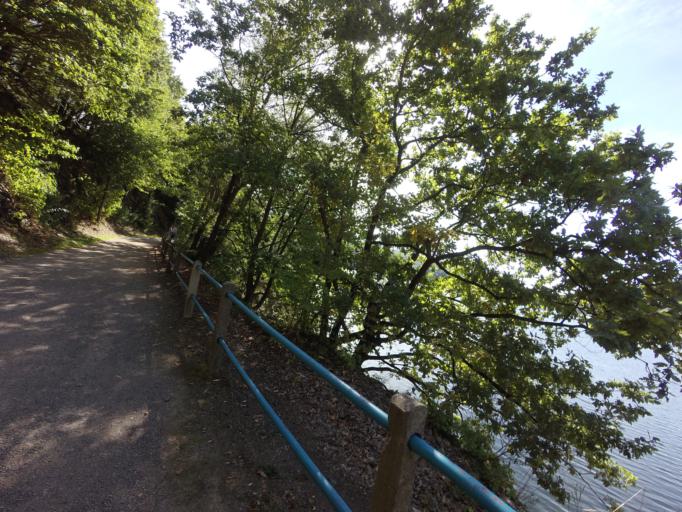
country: DE
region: North Rhine-Westphalia
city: Heimbach
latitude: 50.6421
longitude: 6.4422
